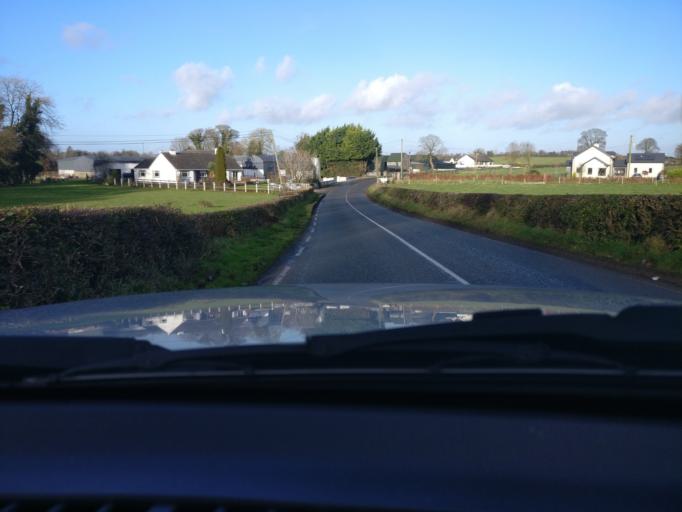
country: IE
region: Leinster
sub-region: Uibh Fhaili
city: Clara
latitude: 53.4040
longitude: -7.5754
